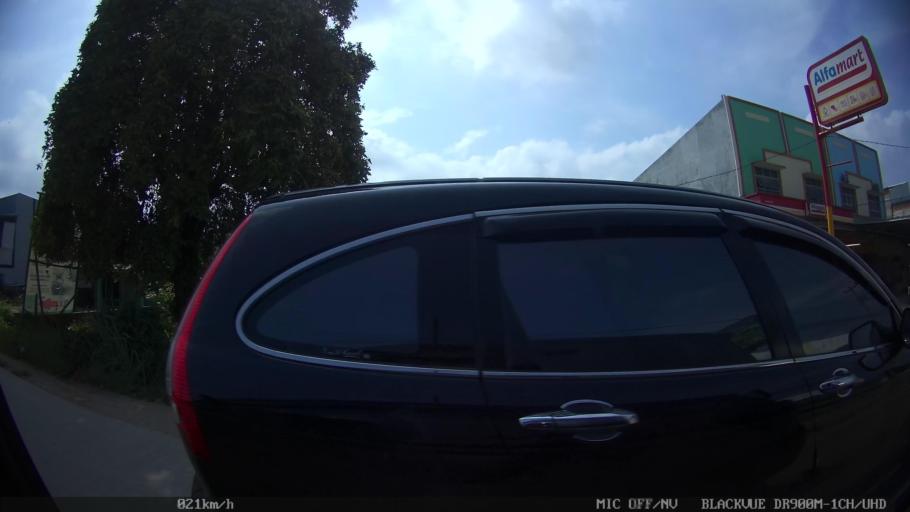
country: ID
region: Lampung
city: Kedaton
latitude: -5.3478
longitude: 105.2664
